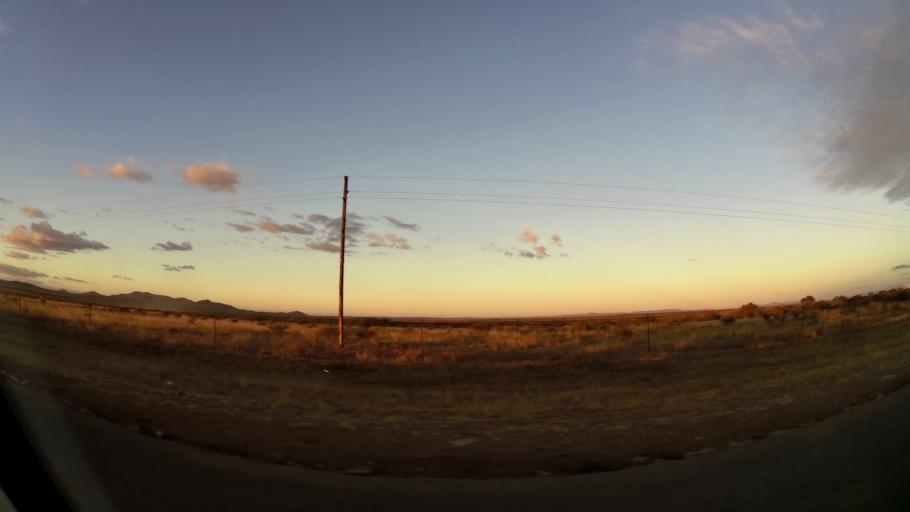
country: ZA
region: Limpopo
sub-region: Capricorn District Municipality
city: Polokwane
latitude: -23.7606
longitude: 29.4738
